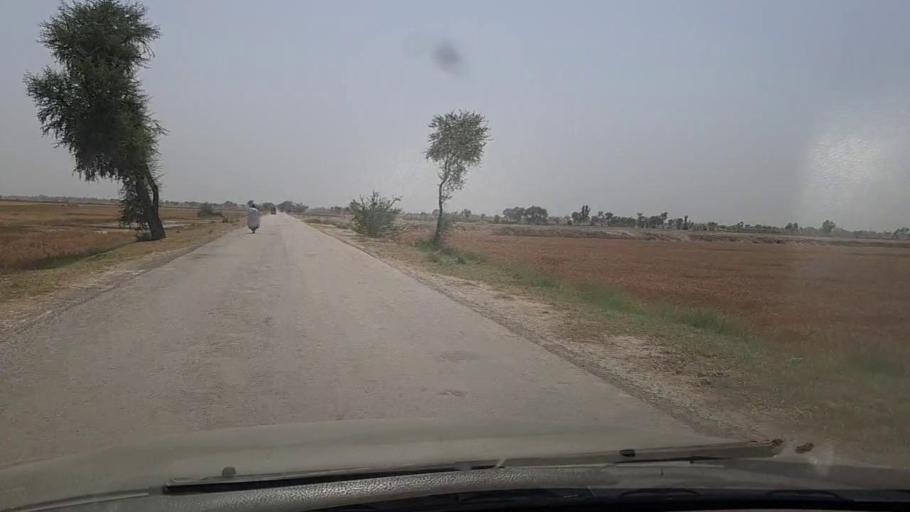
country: PK
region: Sindh
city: Miro Khan
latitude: 27.6982
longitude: 68.0599
